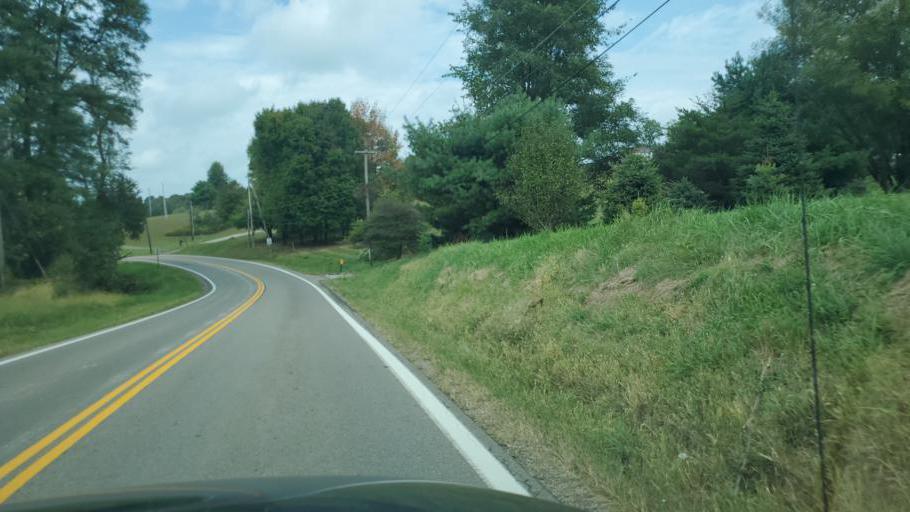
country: US
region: Ohio
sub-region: Perry County
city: Somerset
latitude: 39.9394
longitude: -82.2552
